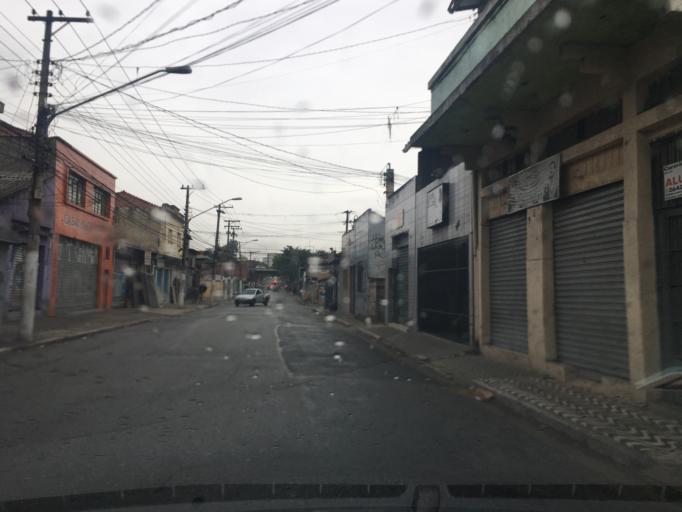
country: BR
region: Sao Paulo
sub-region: Guarulhos
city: Guarulhos
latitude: -23.5128
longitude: -46.5509
